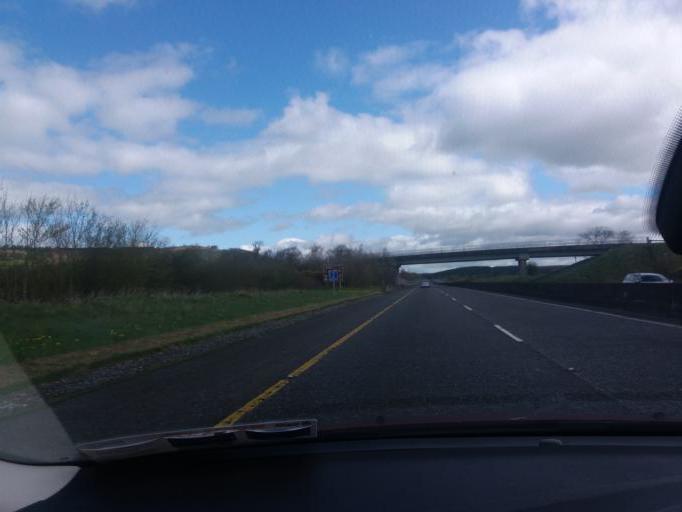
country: IE
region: Munster
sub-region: County Cork
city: Rathcormac
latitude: 52.0966
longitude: -8.2862
